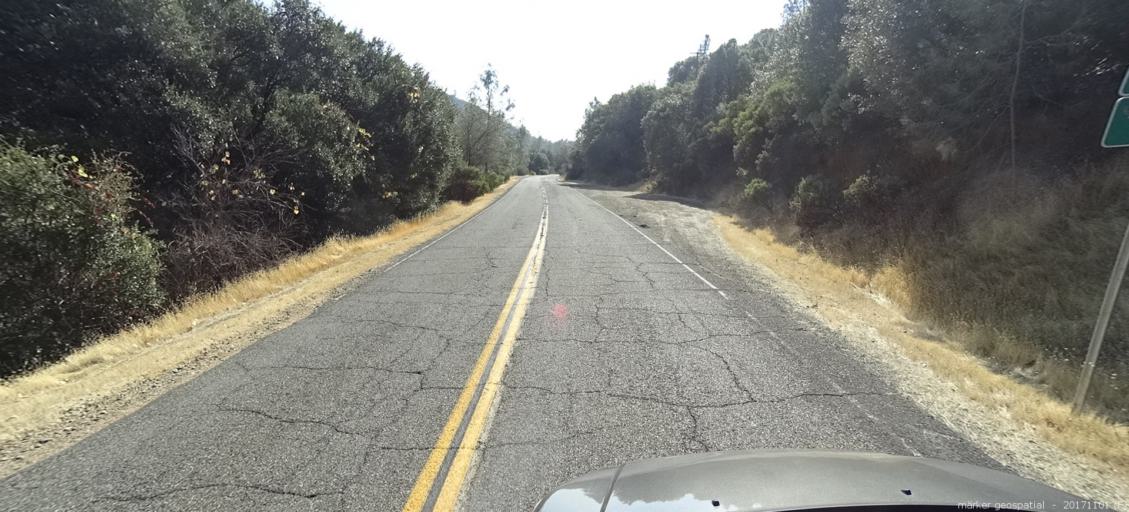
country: US
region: California
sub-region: Shasta County
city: Central Valley (historical)
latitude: 40.7096
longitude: -122.4055
